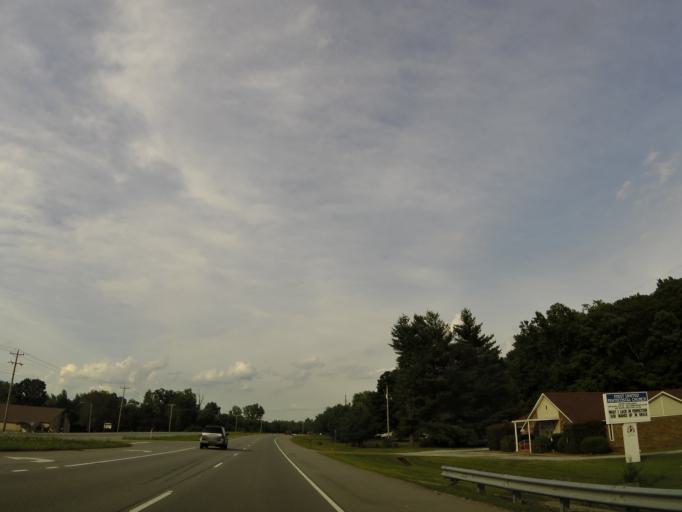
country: US
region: Tennessee
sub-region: Humphreys County
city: Waverly
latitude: 36.0716
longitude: -87.8737
